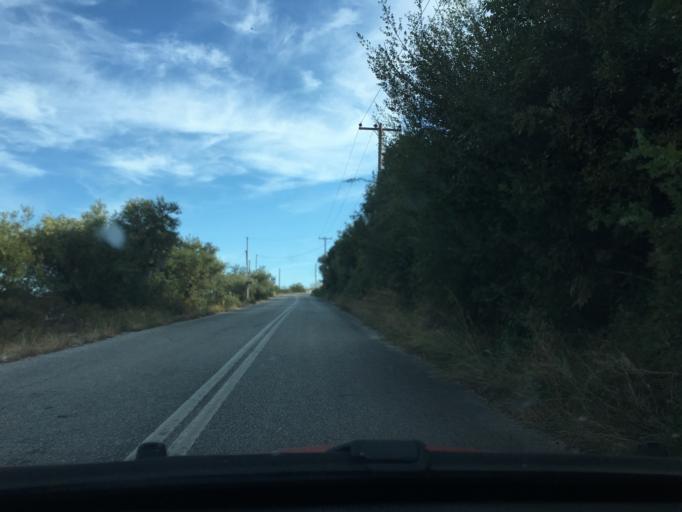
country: GR
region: Central Macedonia
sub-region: Nomos Chalkidikis
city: Agios Nikolaos
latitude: 40.3292
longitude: 23.7051
